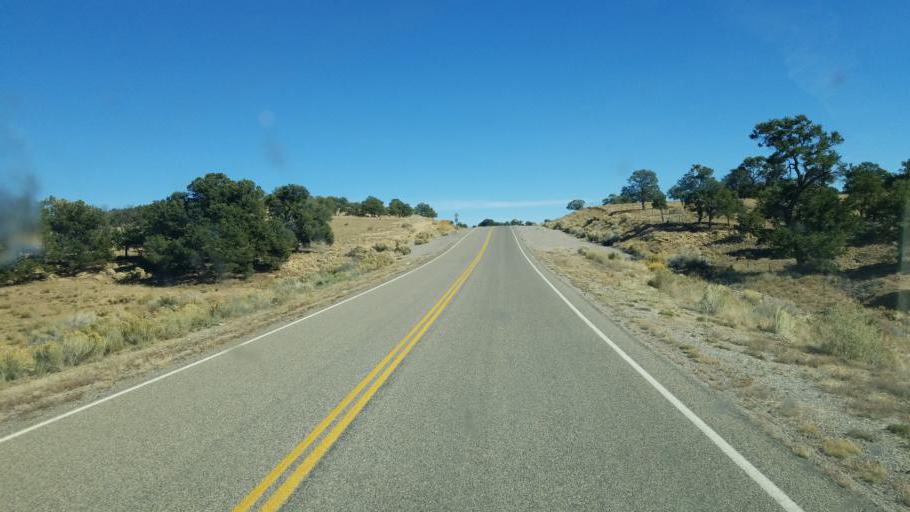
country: US
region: New Mexico
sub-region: McKinley County
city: Crownpoint
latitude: 35.5585
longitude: -108.1206
